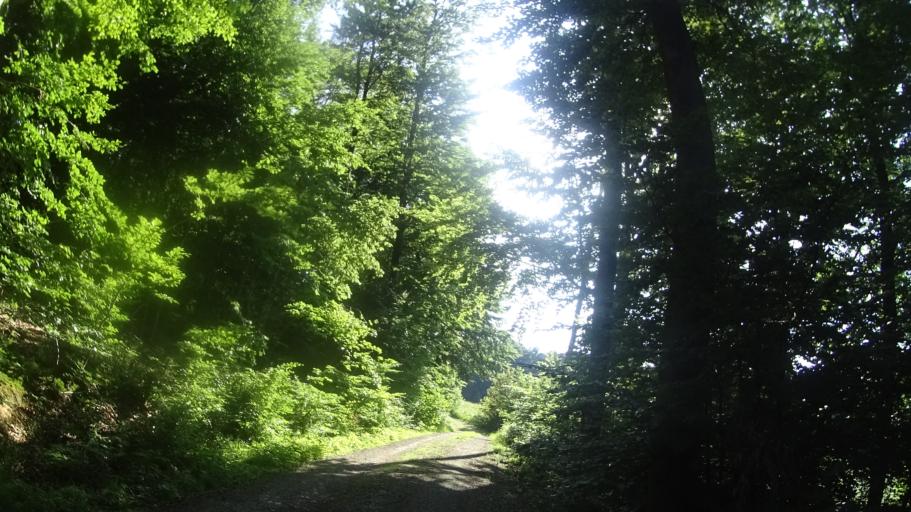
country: DE
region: Lower Saxony
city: Elbe
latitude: 52.1009
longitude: 10.2628
